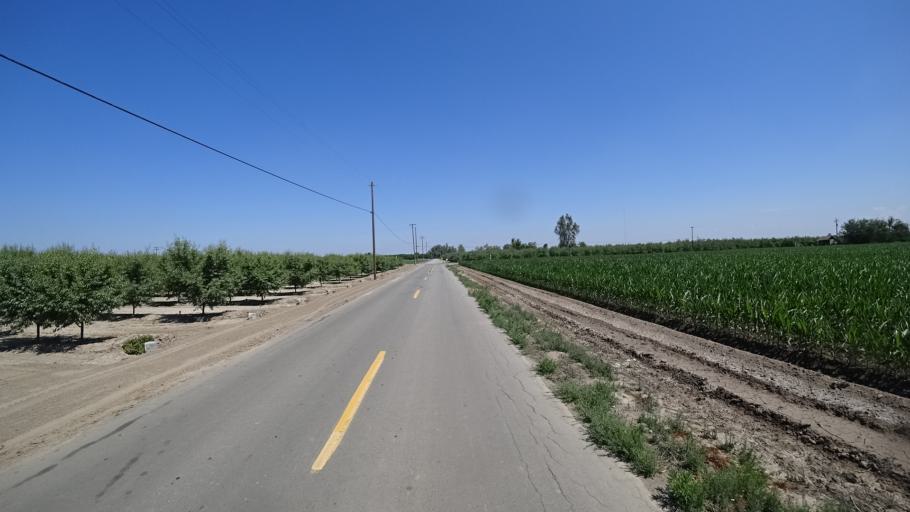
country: US
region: California
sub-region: Fresno County
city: Laton
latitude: 36.4367
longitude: -119.6275
